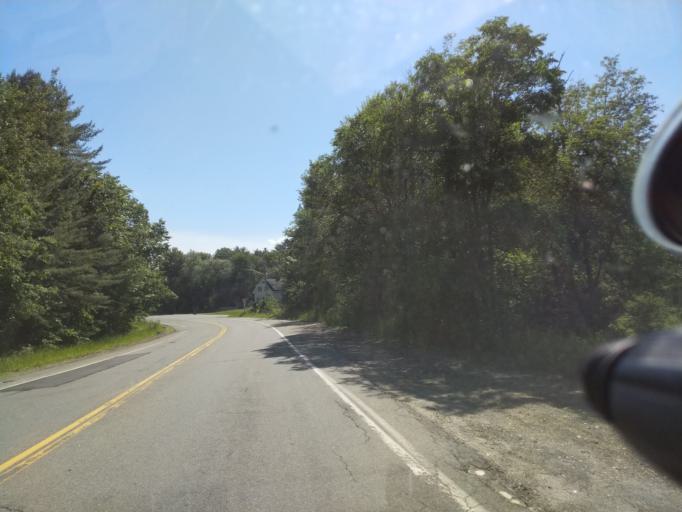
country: US
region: Maine
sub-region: Cumberland County
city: Falmouth
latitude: 43.7208
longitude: -70.2982
